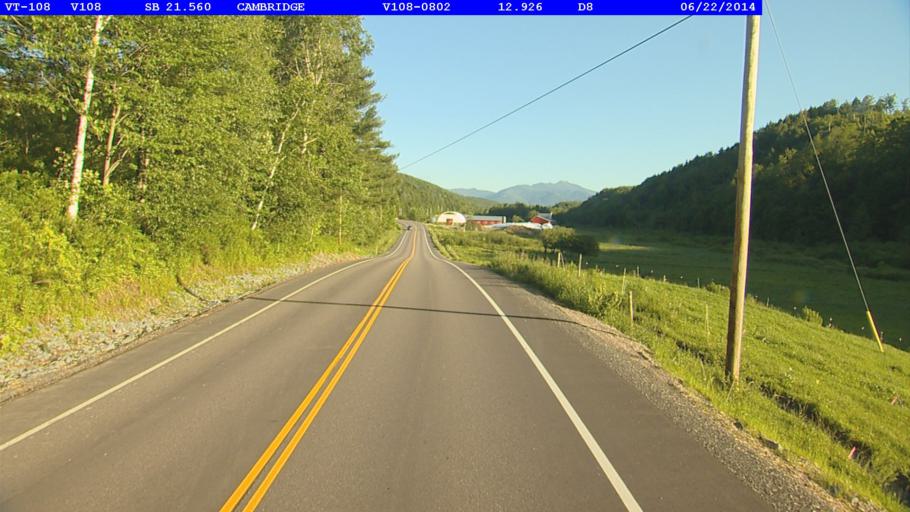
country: US
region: Vermont
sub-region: Lamoille County
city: Johnson
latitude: 44.7010
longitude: -72.8302
